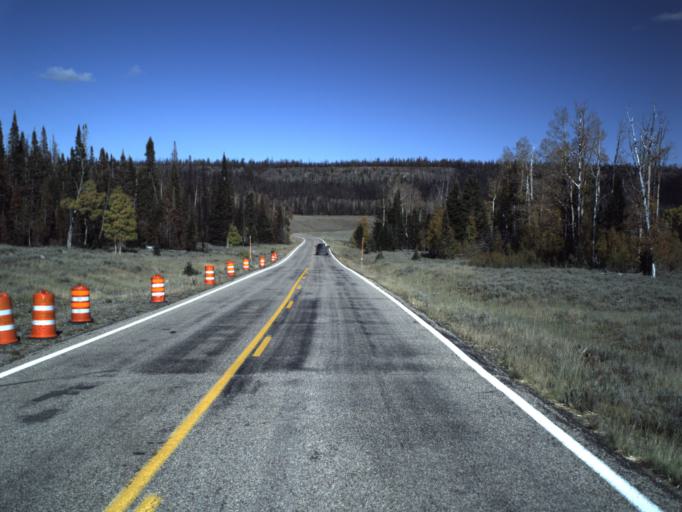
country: US
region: Utah
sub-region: Iron County
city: Parowan
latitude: 37.6611
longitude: -112.7341
